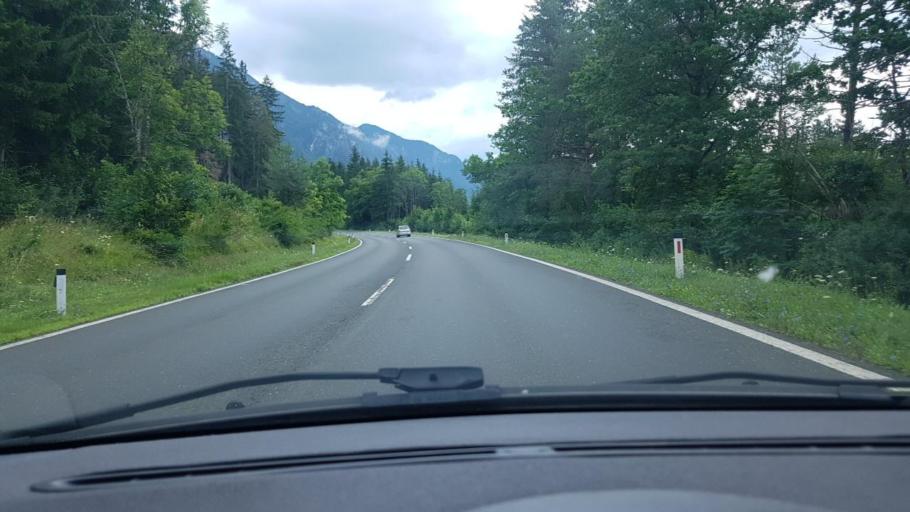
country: AT
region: Carinthia
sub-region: Politischer Bezirk Hermagor
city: Hermagor
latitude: 46.6278
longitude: 13.4263
